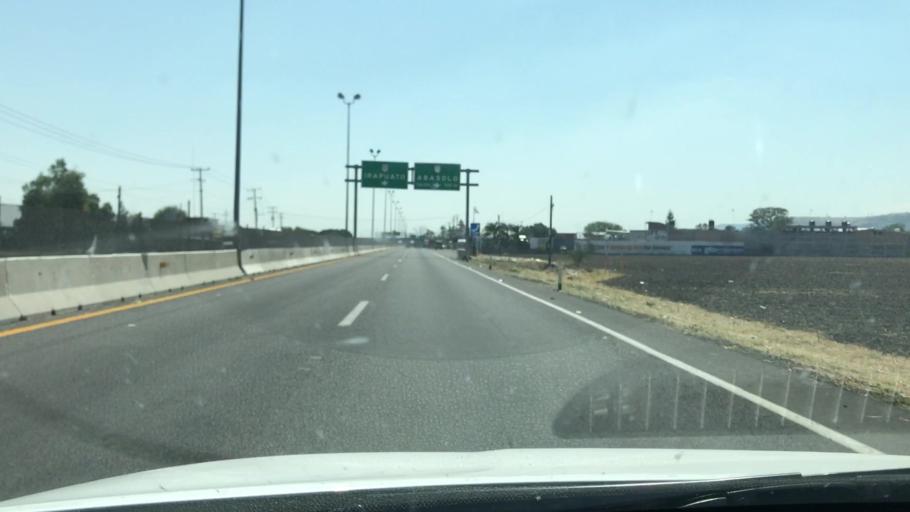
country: MX
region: Guanajuato
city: Abasolo
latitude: 20.4648
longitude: -101.5156
